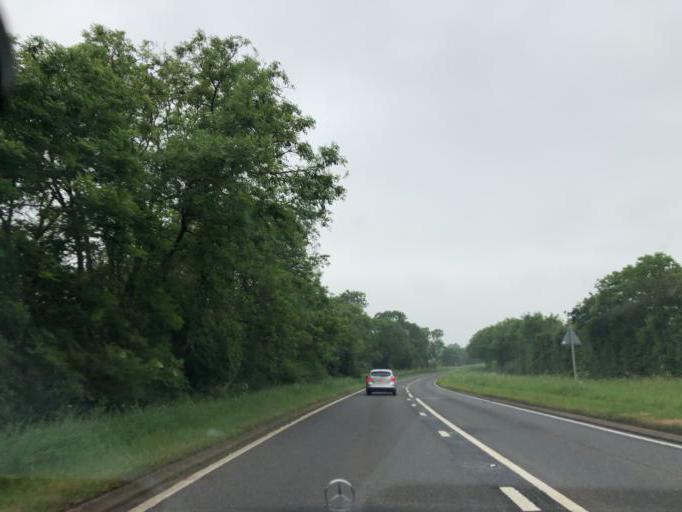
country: GB
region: England
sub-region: Warwickshire
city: Harbury
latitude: 52.2140
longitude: -1.5120
